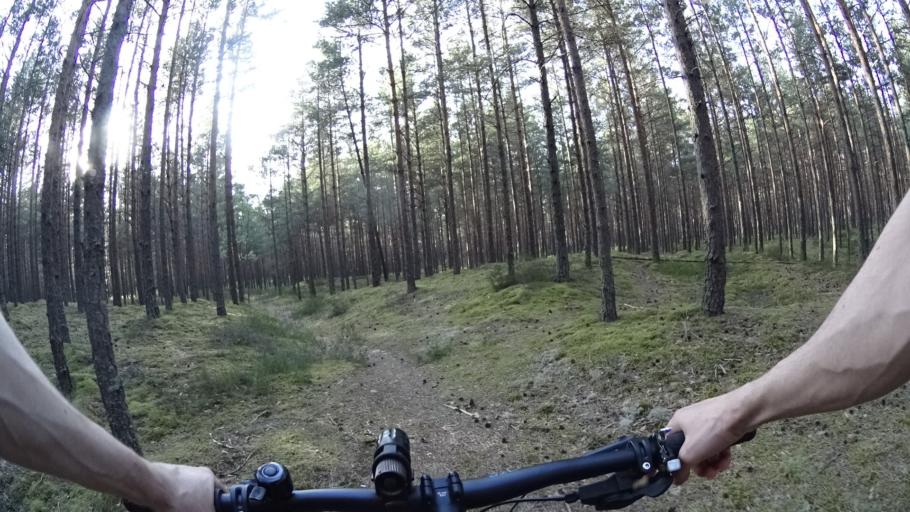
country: LV
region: Riga
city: Jaunciems
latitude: 57.0891
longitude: 24.1522
